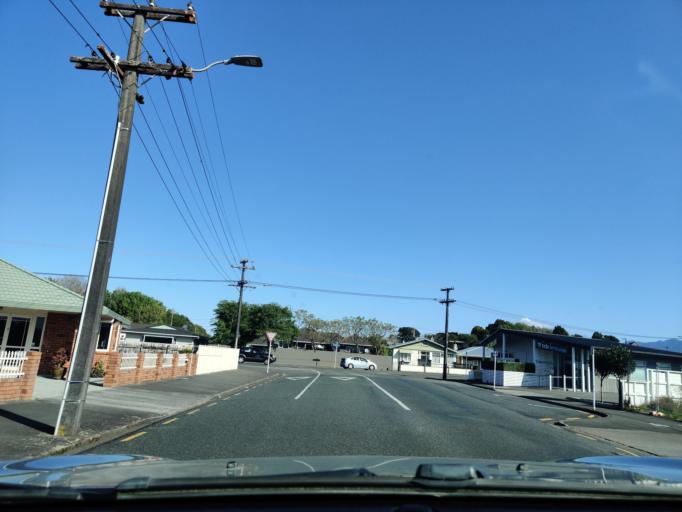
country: NZ
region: Taranaki
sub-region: New Plymouth District
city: New Plymouth
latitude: -39.0735
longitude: 174.0585
